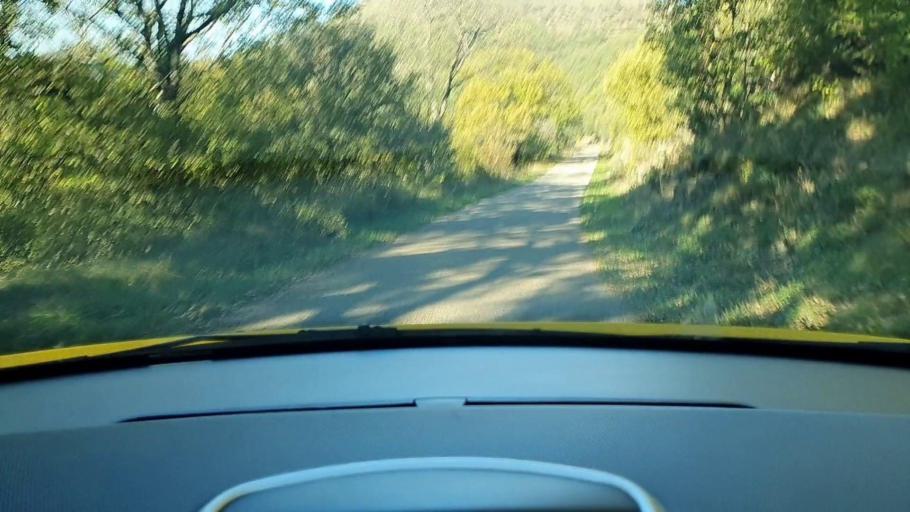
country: FR
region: Languedoc-Roussillon
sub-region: Departement du Gard
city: Sumene
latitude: 43.9771
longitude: 3.7698
